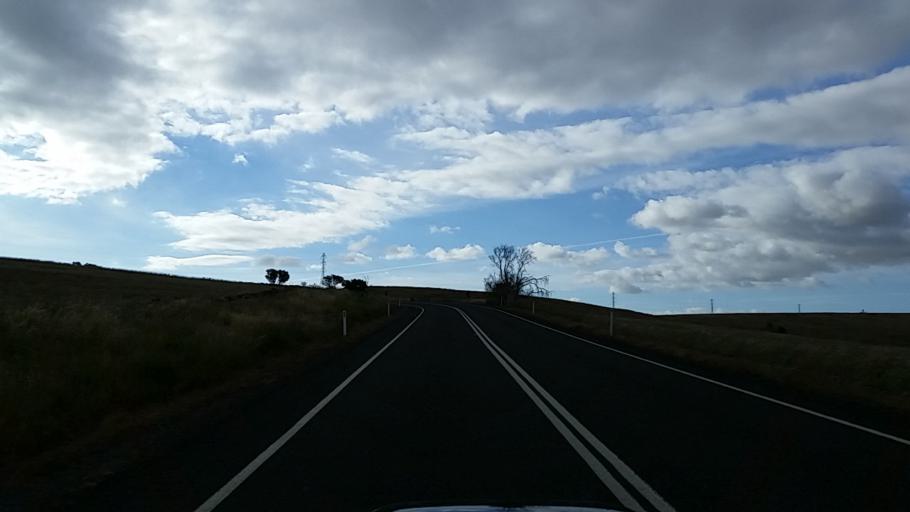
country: AU
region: South Australia
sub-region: Barossa
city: Angaston
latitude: -34.5613
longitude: 139.2040
